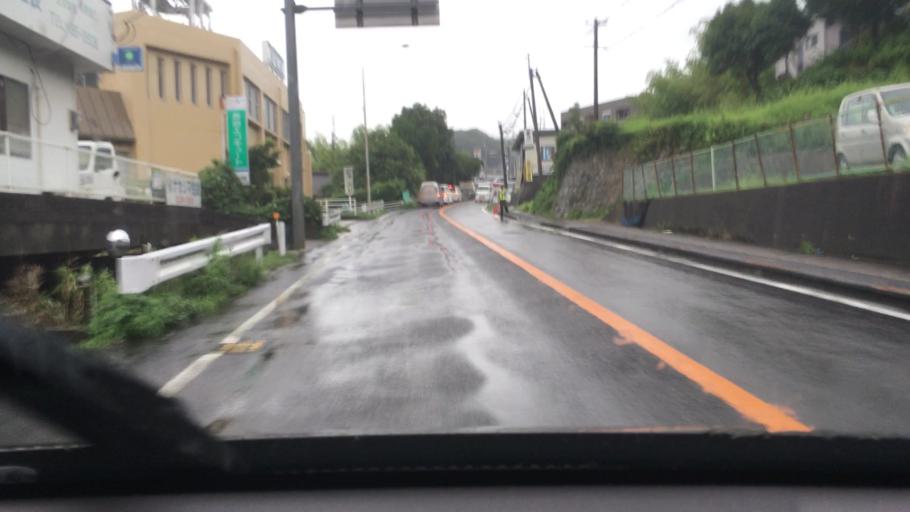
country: JP
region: Nagasaki
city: Sasebo
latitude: 33.1399
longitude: 129.7956
